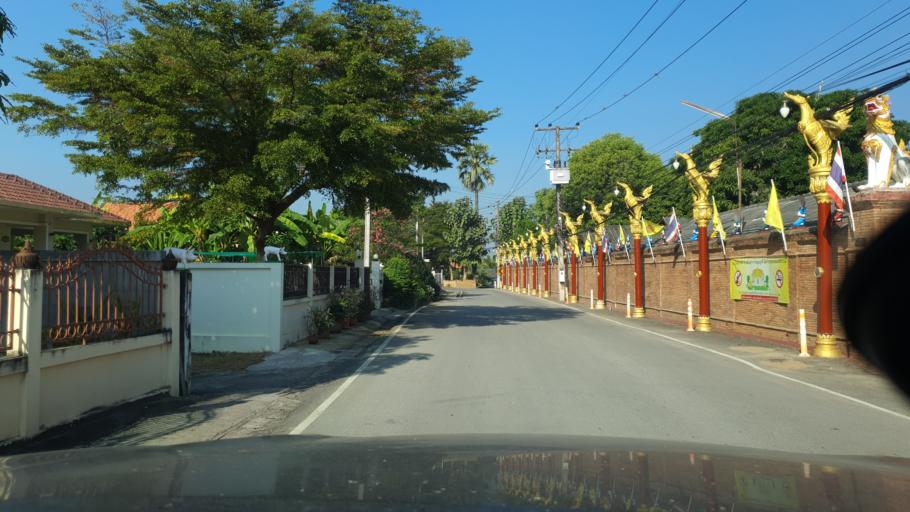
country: TH
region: Chiang Mai
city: San Kamphaeng
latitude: 18.7566
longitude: 99.1576
